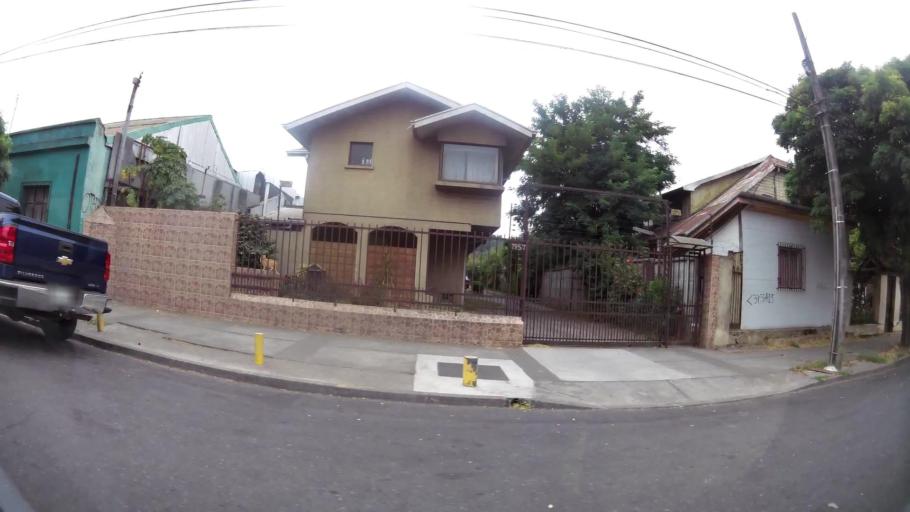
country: CL
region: Biobio
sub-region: Provincia de Concepcion
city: Concepcion
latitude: -36.8157
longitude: -73.0367
